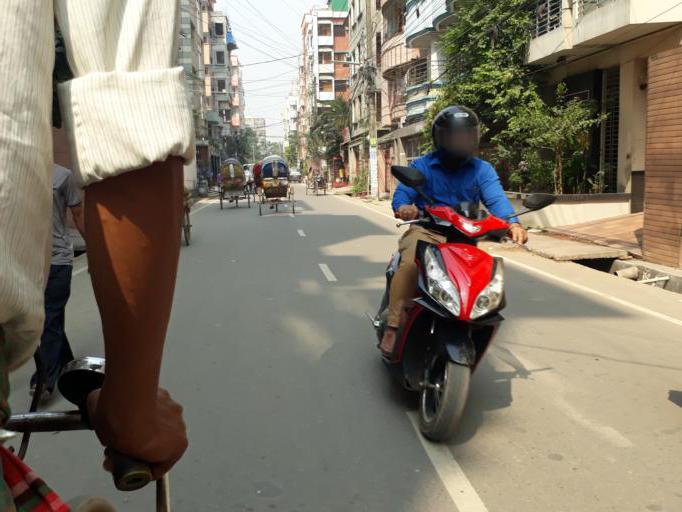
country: BD
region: Dhaka
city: Tungi
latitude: 23.8768
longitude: 90.3867
